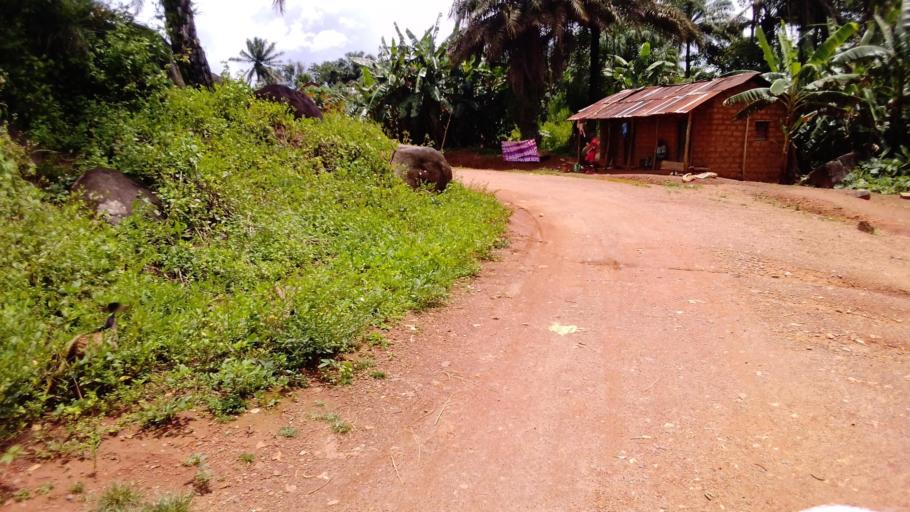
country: SL
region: Eastern Province
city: Koidu
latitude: 8.6731
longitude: -10.9368
